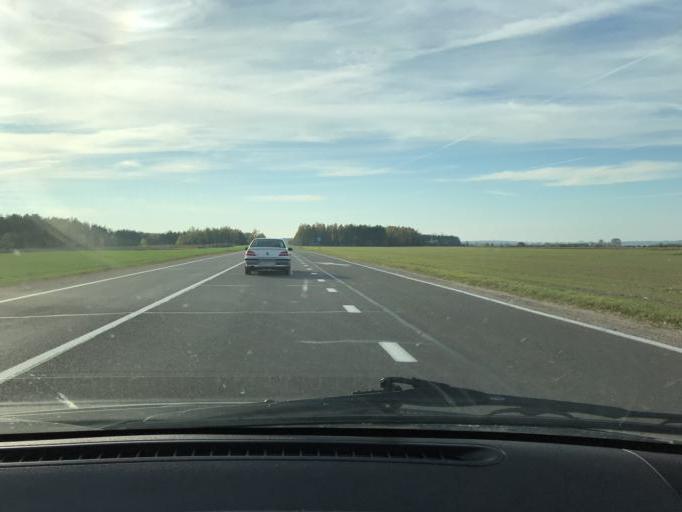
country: BY
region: Brest
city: Horad Pinsk
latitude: 52.1661
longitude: 26.0001
